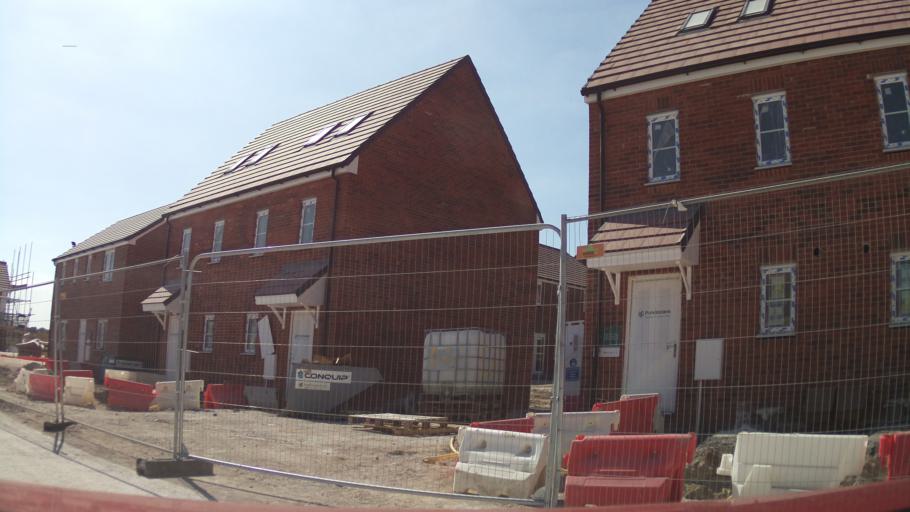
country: GB
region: England
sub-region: Hampshire
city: Andover
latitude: 51.2089
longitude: -1.4397
